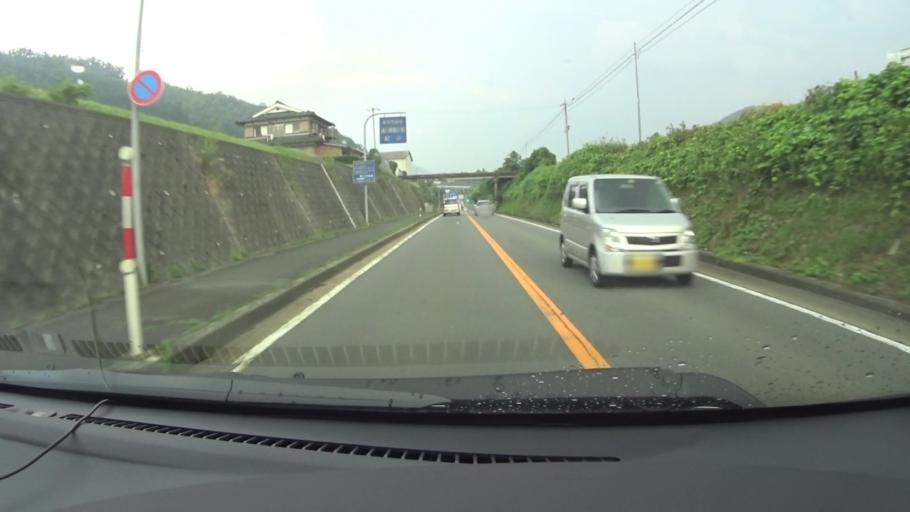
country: JP
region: Kyoto
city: Ayabe
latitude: 35.2239
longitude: 135.4186
